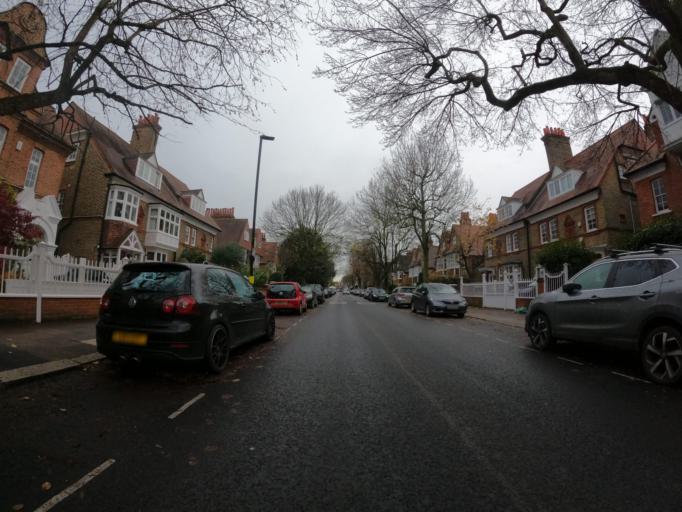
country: GB
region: England
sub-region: Greater London
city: Acton
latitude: 51.4986
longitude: -0.2562
